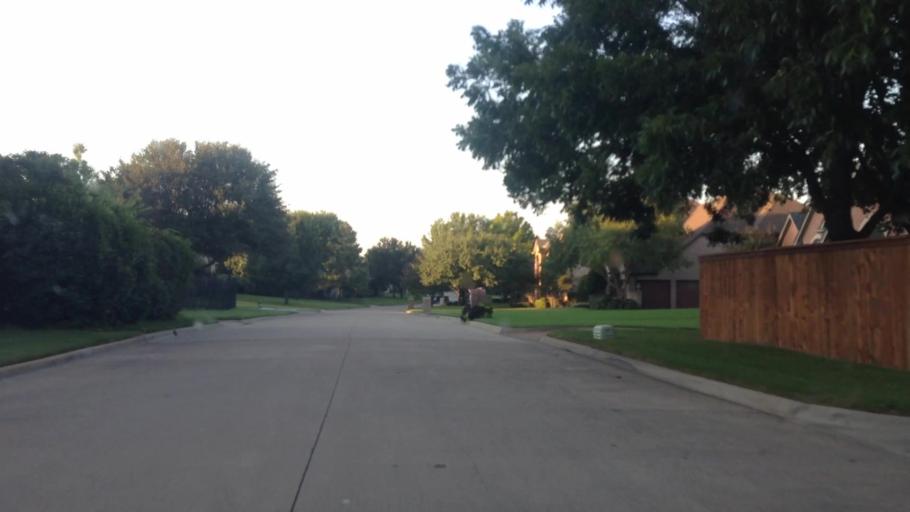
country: US
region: Texas
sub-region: Tarrant County
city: Southlake
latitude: 32.9349
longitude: -97.1280
